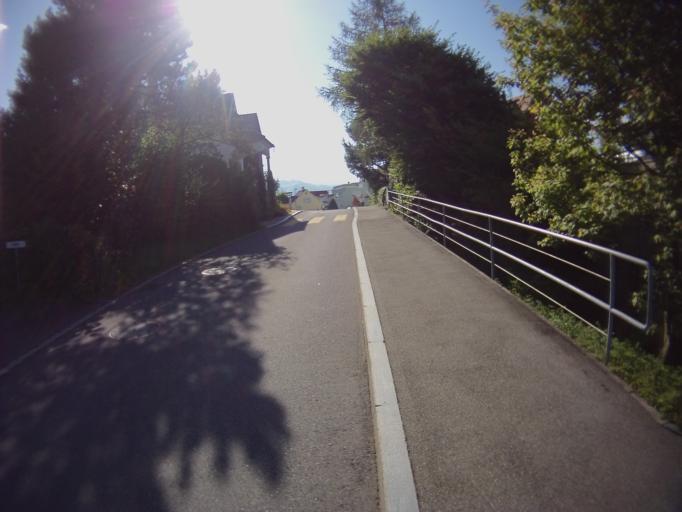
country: CH
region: Zug
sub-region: Zug
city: Unterageri
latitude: 47.1378
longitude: 8.5952
